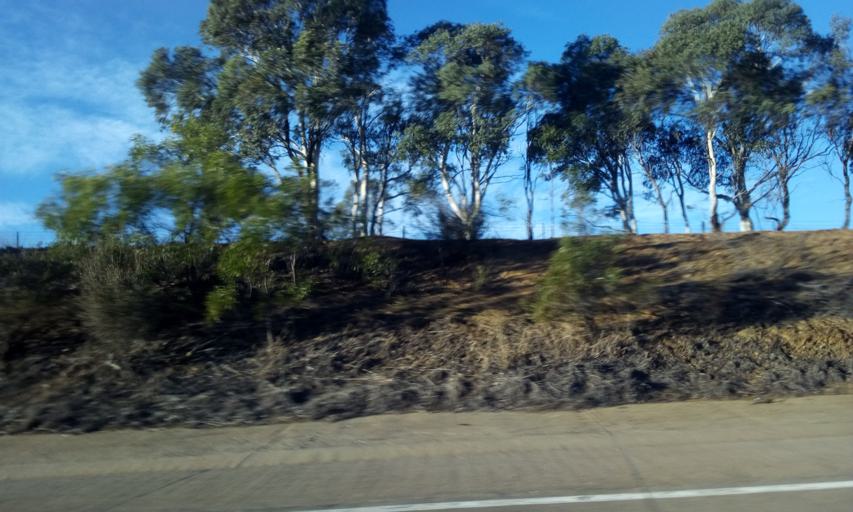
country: AU
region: New South Wales
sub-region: Yass Valley
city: Gundaroo
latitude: -35.1822
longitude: 149.2564
